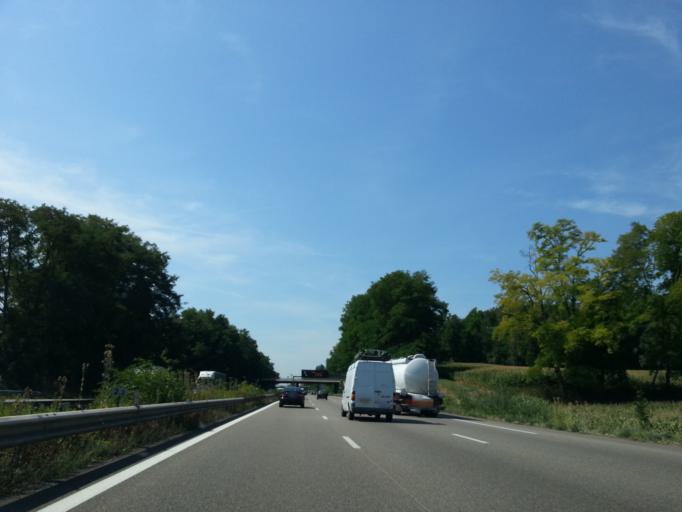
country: FR
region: Alsace
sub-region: Departement du Bas-Rhin
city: Souffelweyersheim
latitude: 48.6395
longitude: 7.7292
